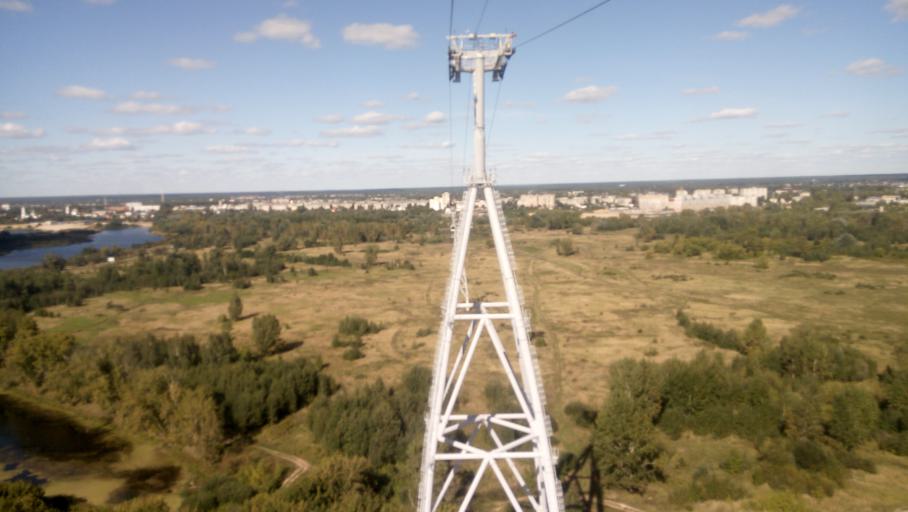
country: RU
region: Nizjnij Novgorod
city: Bor
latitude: 56.3403
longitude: 44.0510
